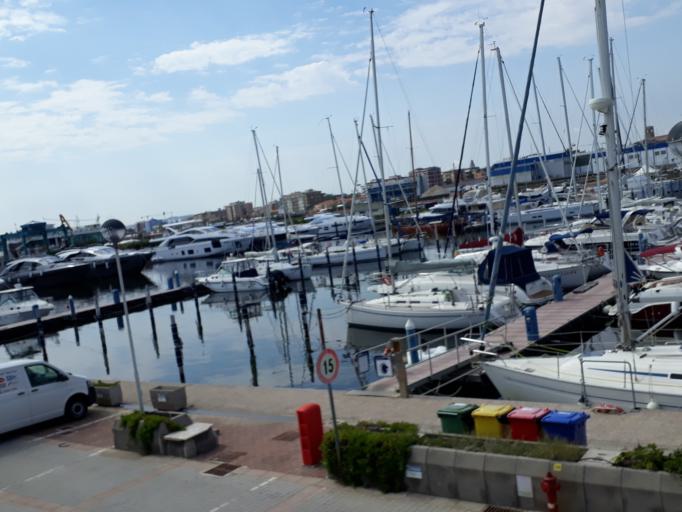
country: IT
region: The Marches
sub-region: Provincia di Pesaro e Urbino
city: Fano
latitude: 43.8539
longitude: 13.0201
